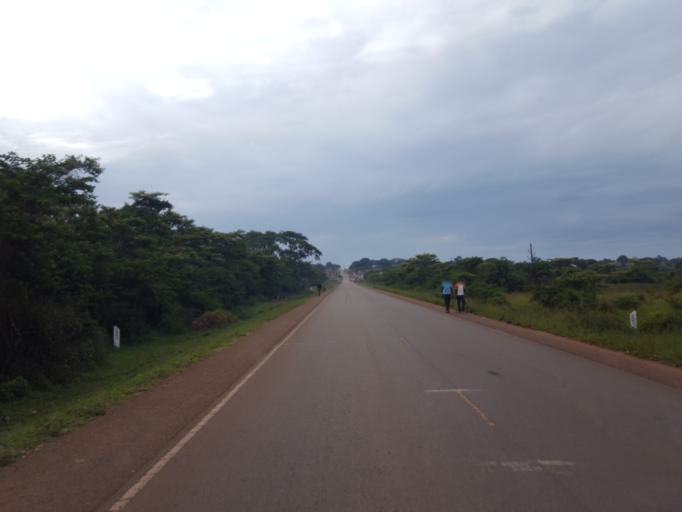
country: UG
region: Central Region
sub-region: Kyankwanzi District
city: Kyankwanzi
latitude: 1.1299
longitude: 31.5913
